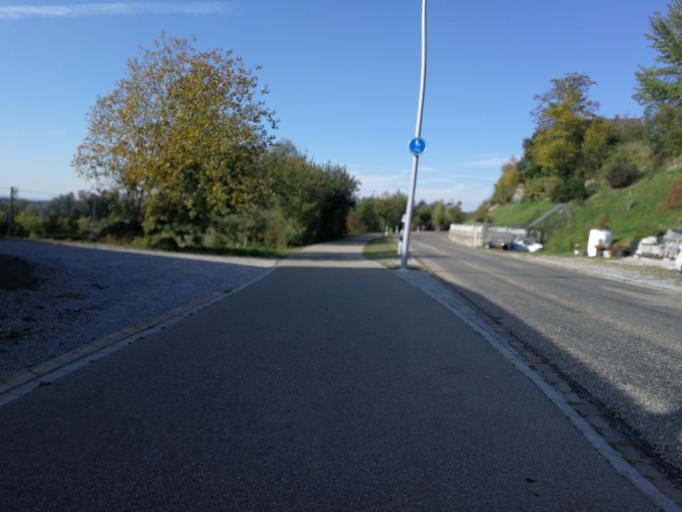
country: CH
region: Zurich
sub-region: Bezirk Hinwil
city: Hadlikon
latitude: 47.2901
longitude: 8.8540
